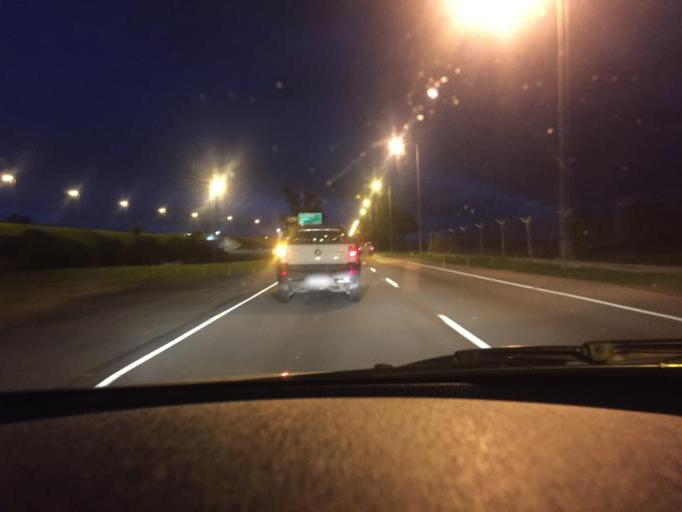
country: AR
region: Cordoba
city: Villa Allende
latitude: -31.3049
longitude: -64.2224
